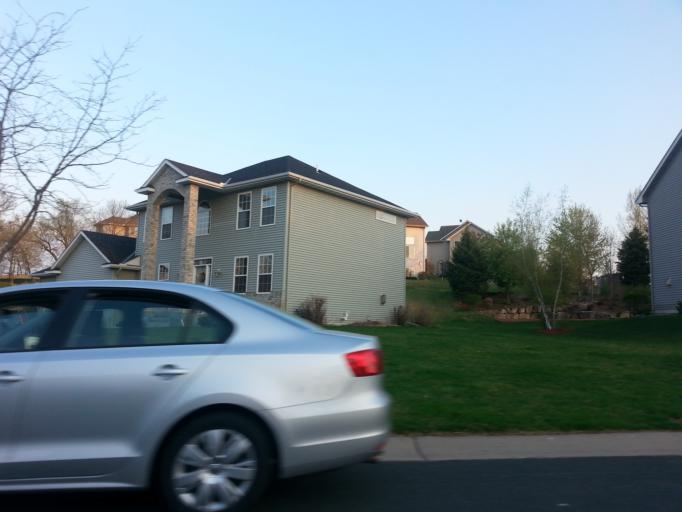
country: US
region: Minnesota
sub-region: Scott County
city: Prior Lake
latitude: 44.7420
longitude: -93.4206
